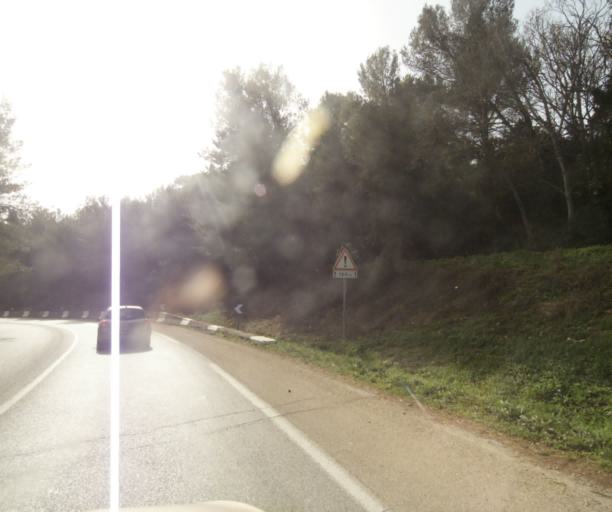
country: FR
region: Provence-Alpes-Cote d'Azur
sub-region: Departement des Bouches-du-Rhone
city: Bouc-Bel-Air
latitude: 43.4906
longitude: 5.4066
